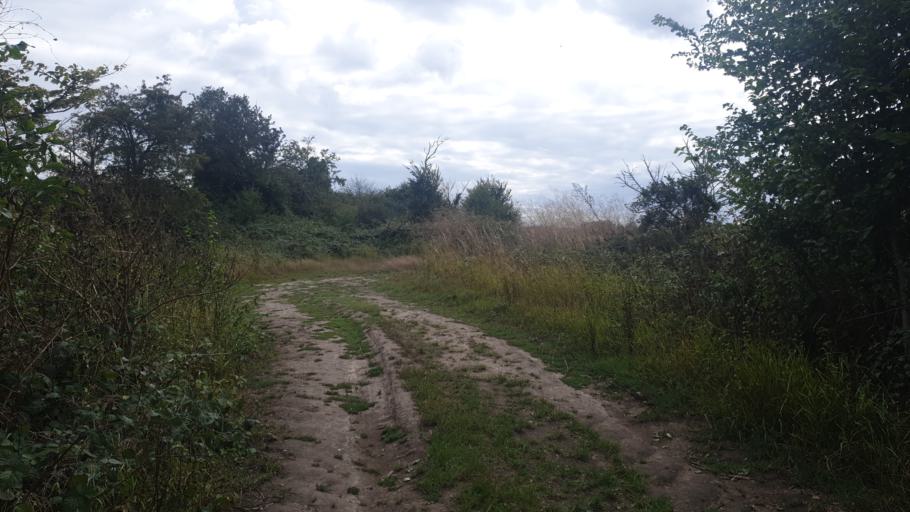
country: GB
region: England
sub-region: Essex
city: Frinton-on-Sea
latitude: 51.8482
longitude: 1.2360
